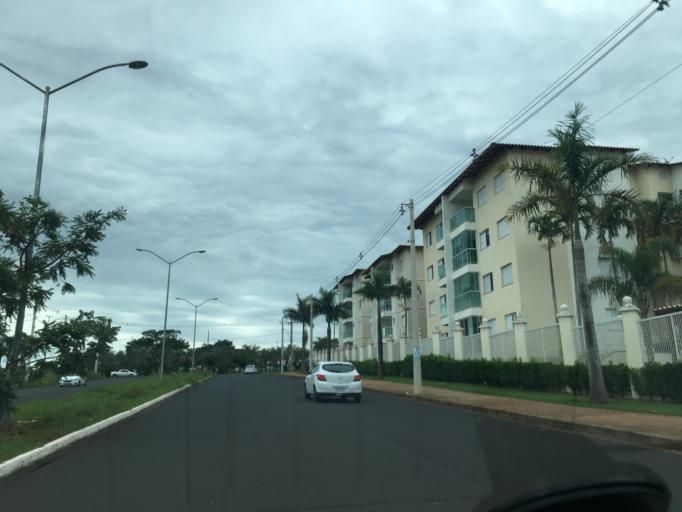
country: BR
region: Minas Gerais
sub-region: Uberlandia
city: Uberlandia
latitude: -18.8810
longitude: -48.2434
